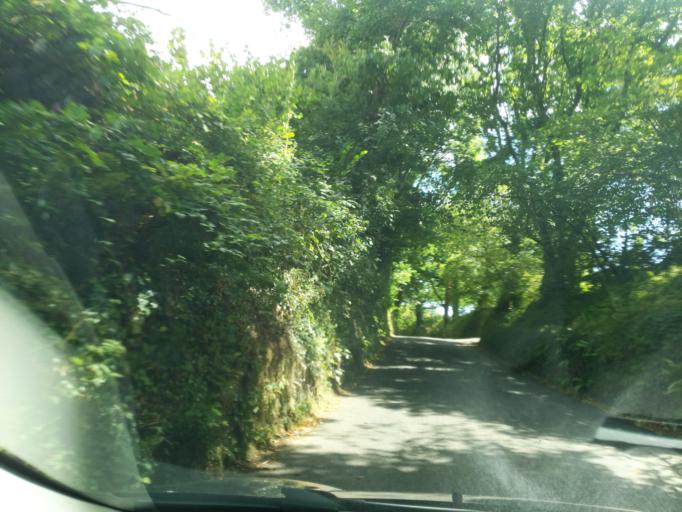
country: GB
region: England
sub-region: Devon
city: Modbury
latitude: 50.3626
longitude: -3.8985
